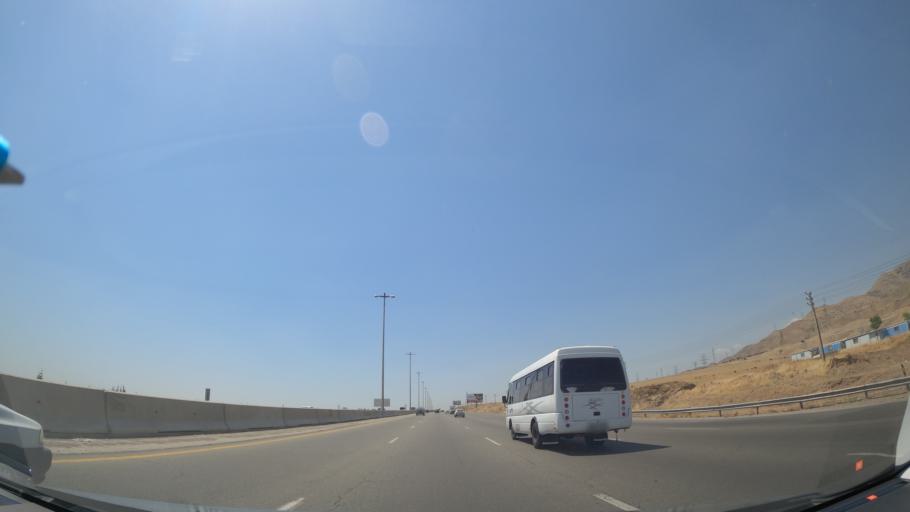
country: IR
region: Tehran
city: Shahr-e Qods
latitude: 35.7657
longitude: 51.0553
